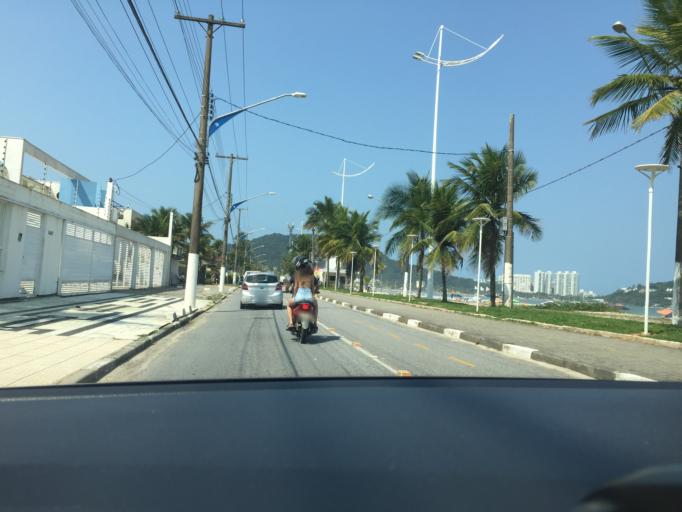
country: BR
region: Sao Paulo
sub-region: Guaruja
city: Guaruja
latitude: -23.9848
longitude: -46.2181
